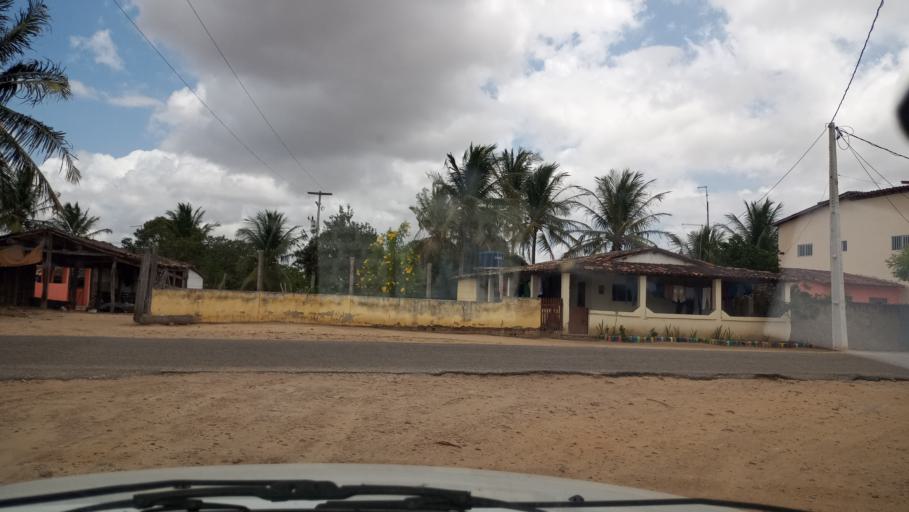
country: BR
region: Rio Grande do Norte
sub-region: Santo Antonio
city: Santo Antonio
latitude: -6.2130
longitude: -35.4638
